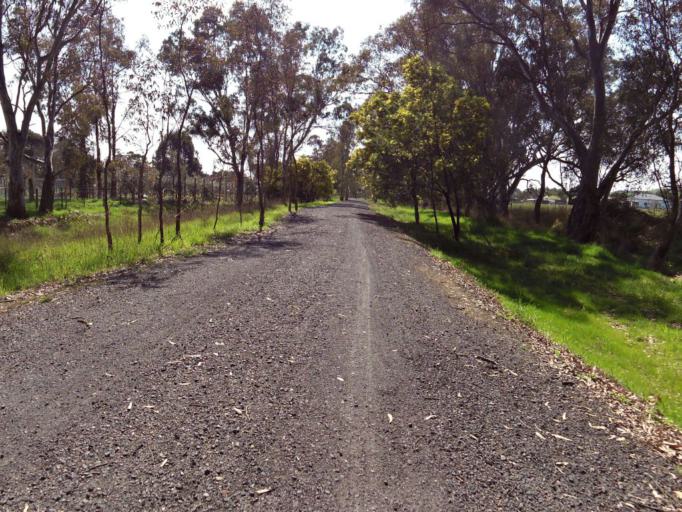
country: AU
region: Victoria
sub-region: Murrindindi
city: Alexandra
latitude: -37.1075
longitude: 145.6144
